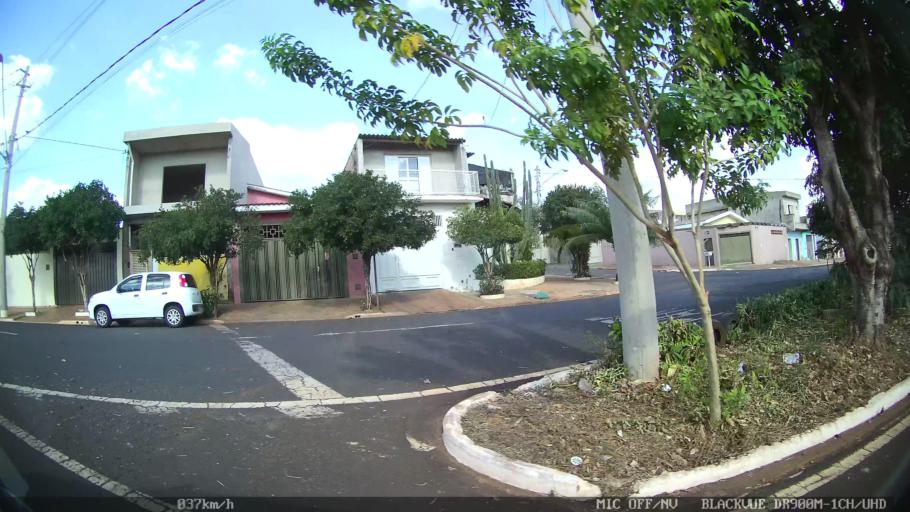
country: BR
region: Sao Paulo
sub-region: Ribeirao Preto
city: Ribeirao Preto
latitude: -21.1955
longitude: -47.8497
